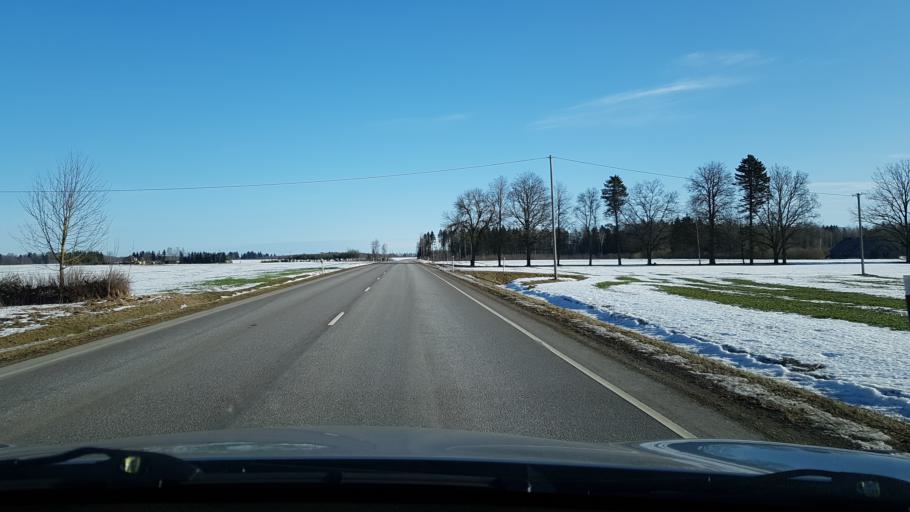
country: EE
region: Viljandimaa
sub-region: Vohma linn
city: Vohma
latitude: 58.6364
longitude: 25.7506
